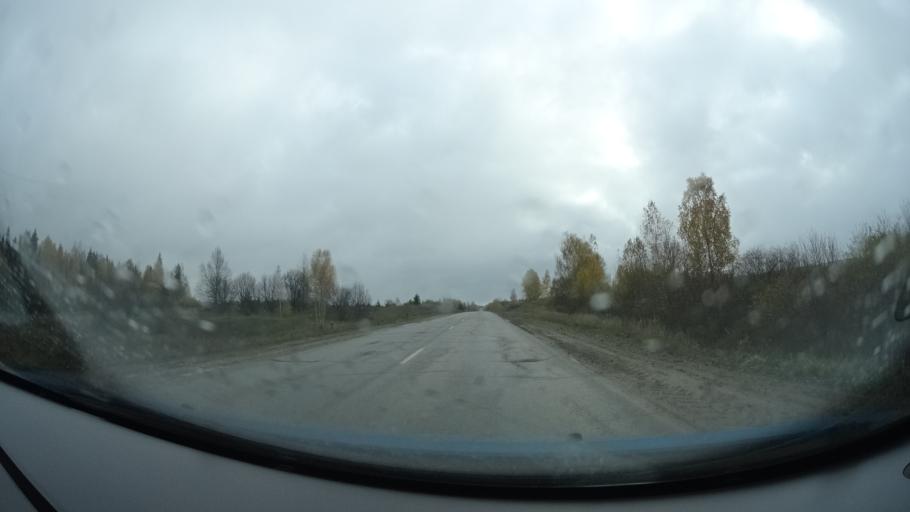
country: RU
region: Perm
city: Chernushka
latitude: 56.7487
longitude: 56.1550
